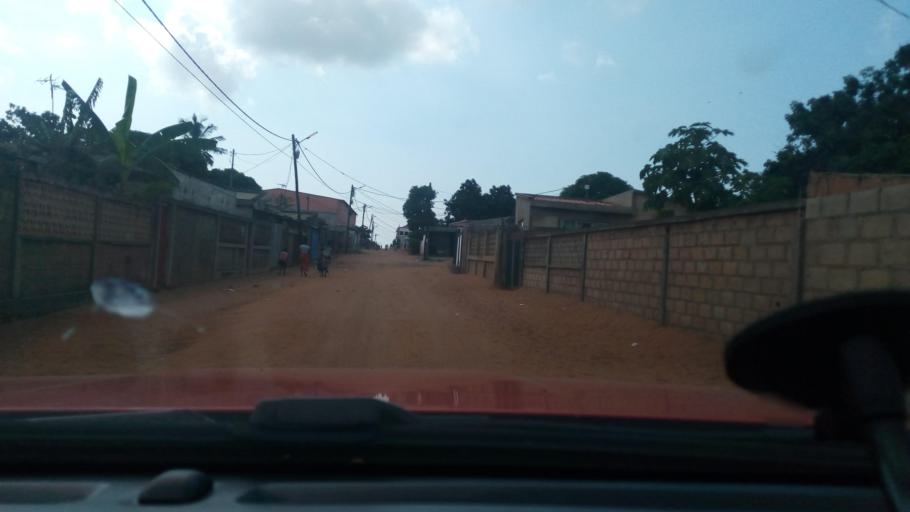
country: MZ
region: Maputo City
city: Maputo
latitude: -25.9221
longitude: 32.5924
